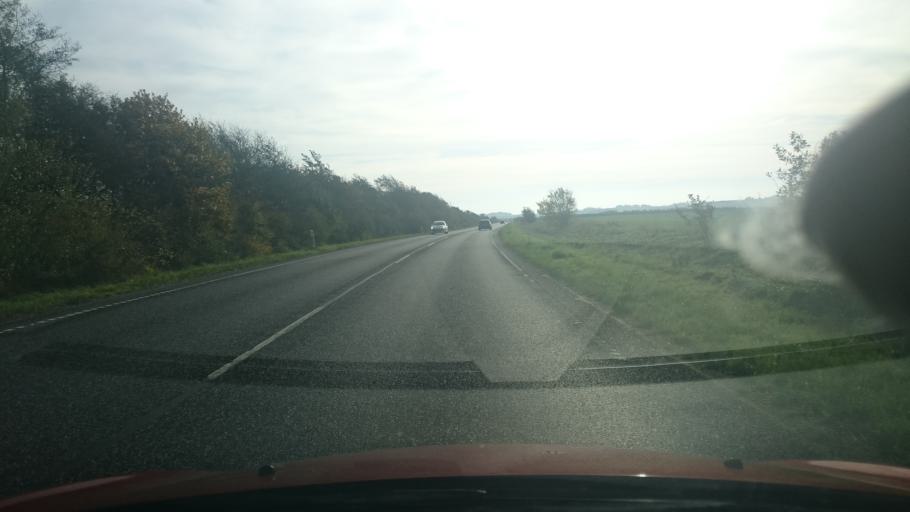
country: DK
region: Central Jutland
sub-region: Randers Kommune
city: Assentoft
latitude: 56.4389
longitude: 10.1234
